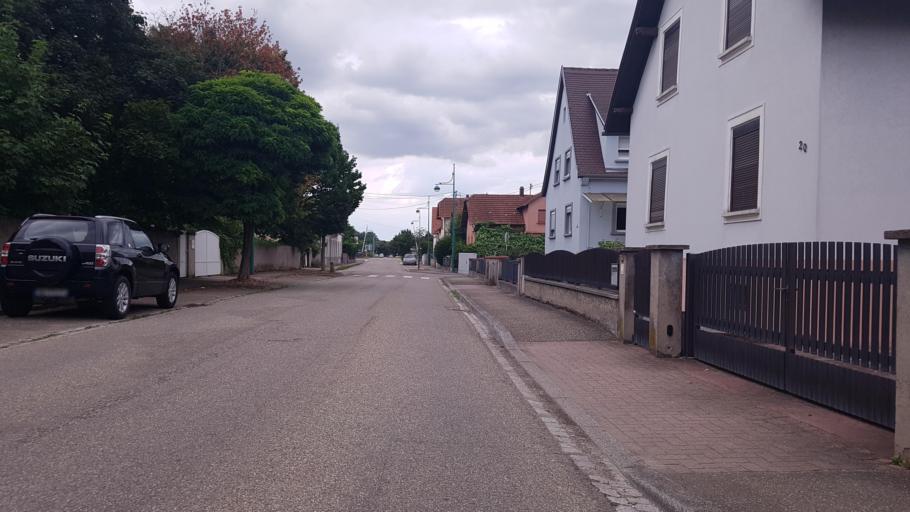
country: FR
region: Alsace
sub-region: Departement du Bas-Rhin
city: Gambsheim
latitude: 48.6961
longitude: 7.8839
